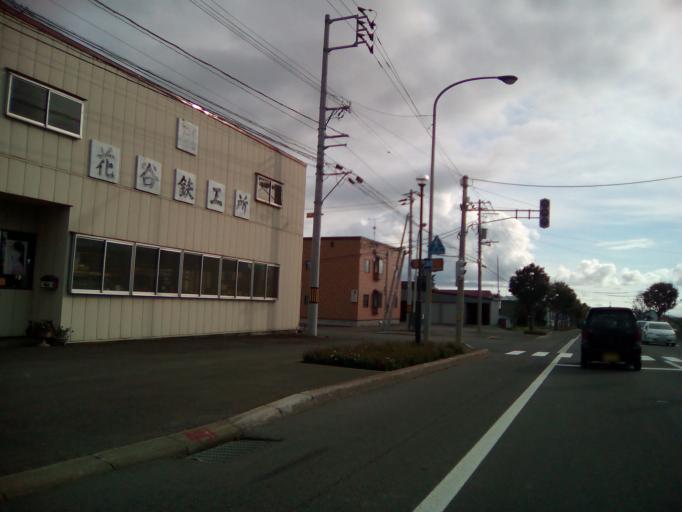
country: JP
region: Hokkaido
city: Niseko Town
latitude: 42.7342
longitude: 140.8740
